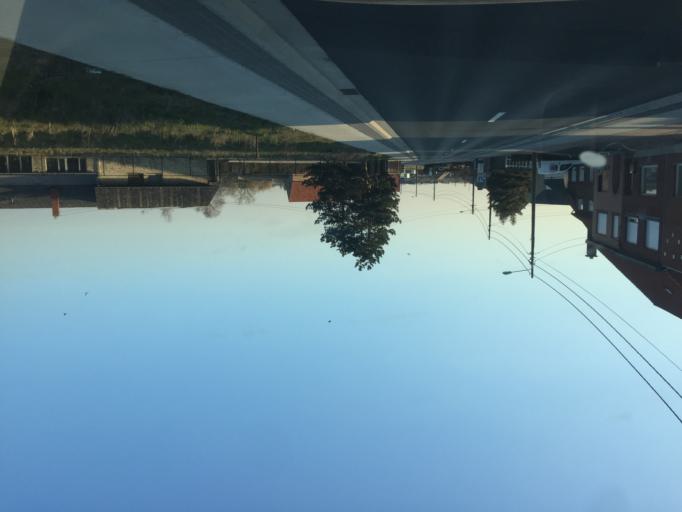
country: BE
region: Flanders
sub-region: Provincie West-Vlaanderen
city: Meulebeke
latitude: 50.9378
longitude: 3.2978
